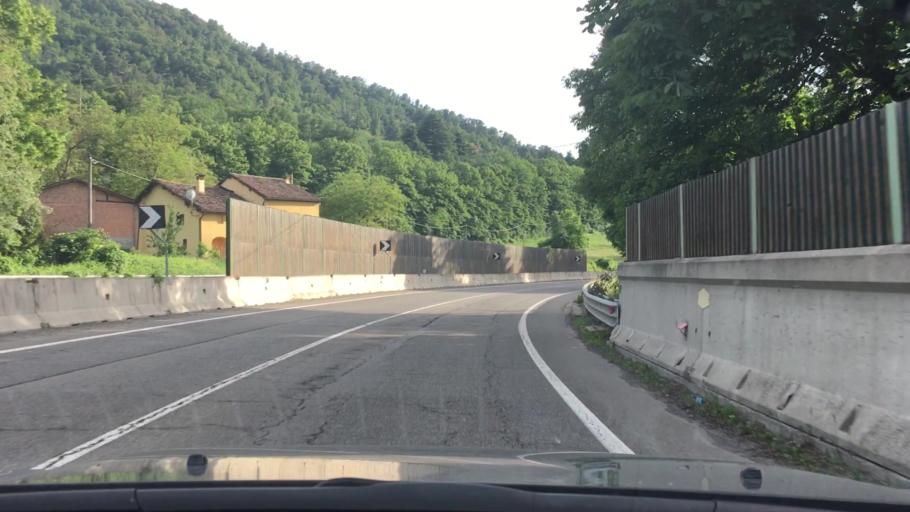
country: IT
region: Emilia-Romagna
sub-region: Provincia di Bologna
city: Sasso Marconi
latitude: 44.3906
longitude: 11.2578
